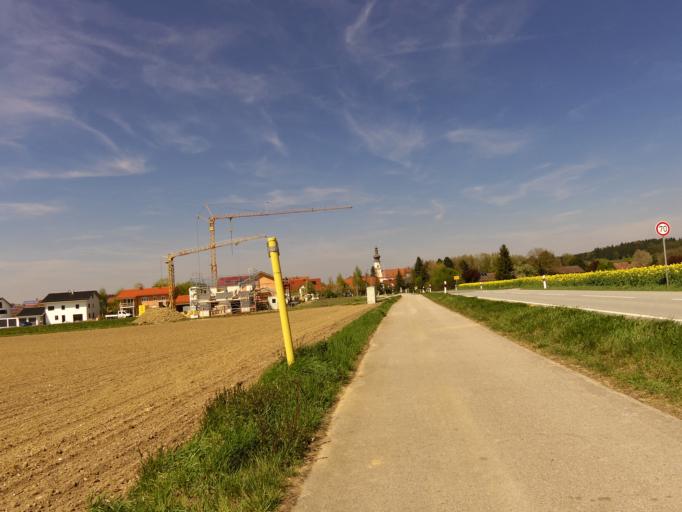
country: DE
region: Bavaria
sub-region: Upper Bavaria
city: Bockhorn
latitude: 48.3106
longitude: 11.9865
